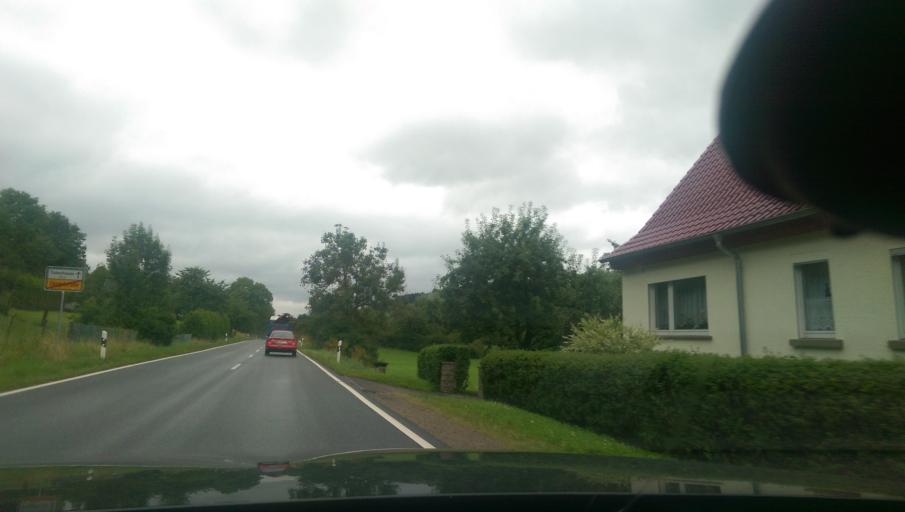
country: DE
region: Hesse
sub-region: Regierungsbezirk Kassel
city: Grossalmerode
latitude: 51.2520
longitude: 9.8268
